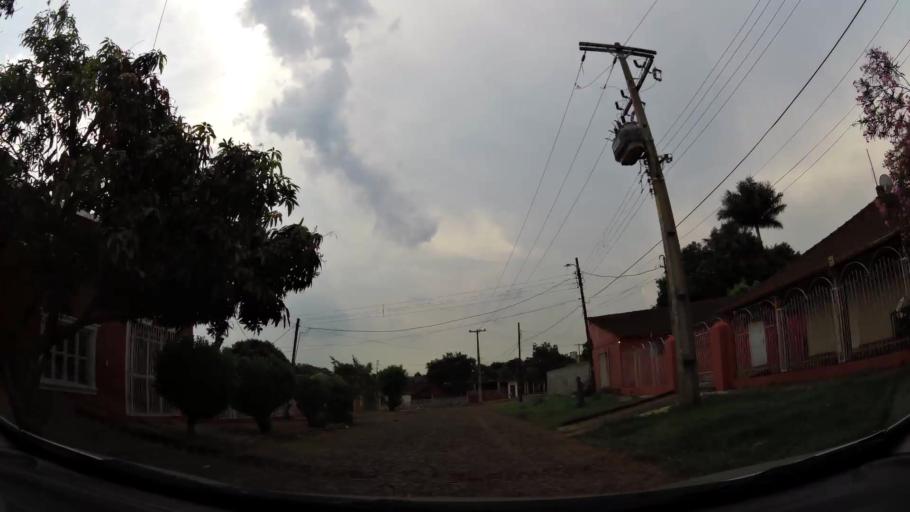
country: PY
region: Alto Parana
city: Presidente Franco
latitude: -25.5427
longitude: -54.6116
